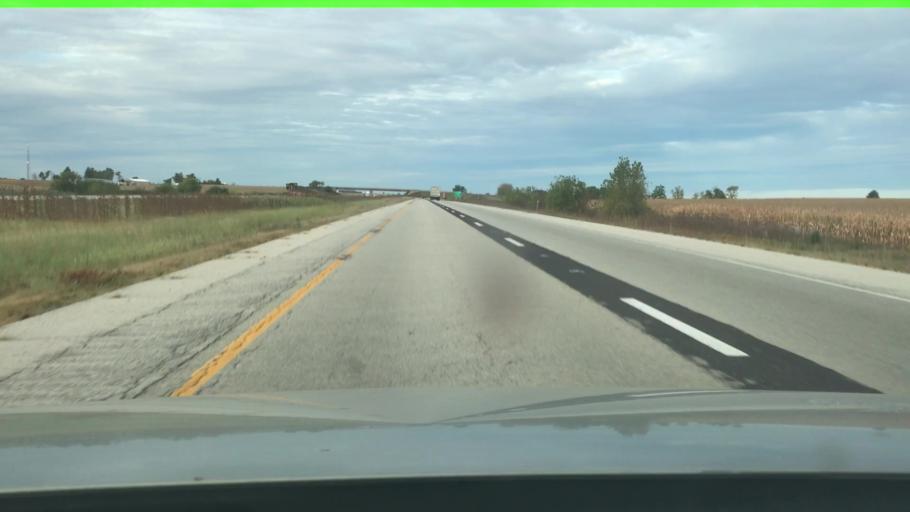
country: US
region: Illinois
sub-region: Livingston County
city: Odell
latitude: 41.0221
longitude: -88.5193
